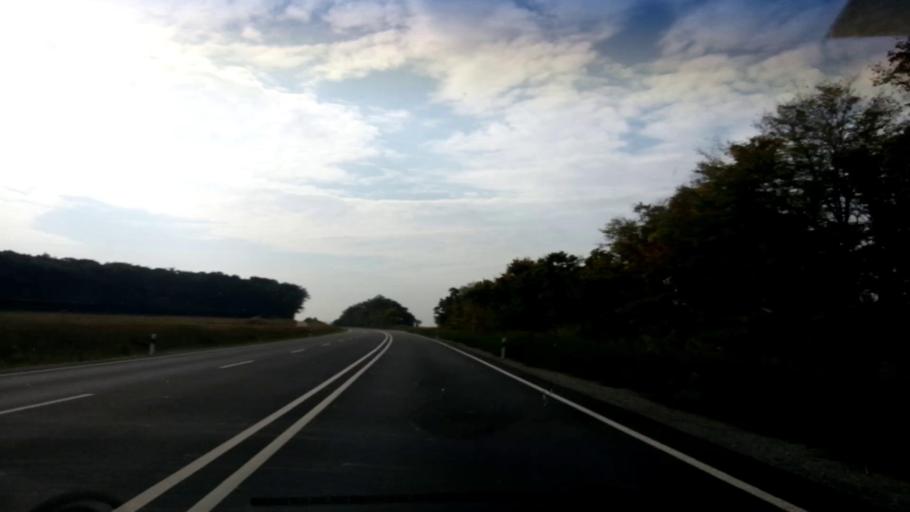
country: DE
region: Bavaria
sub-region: Regierungsbezirk Unterfranken
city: Gerolzhofen
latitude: 49.8846
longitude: 10.3561
